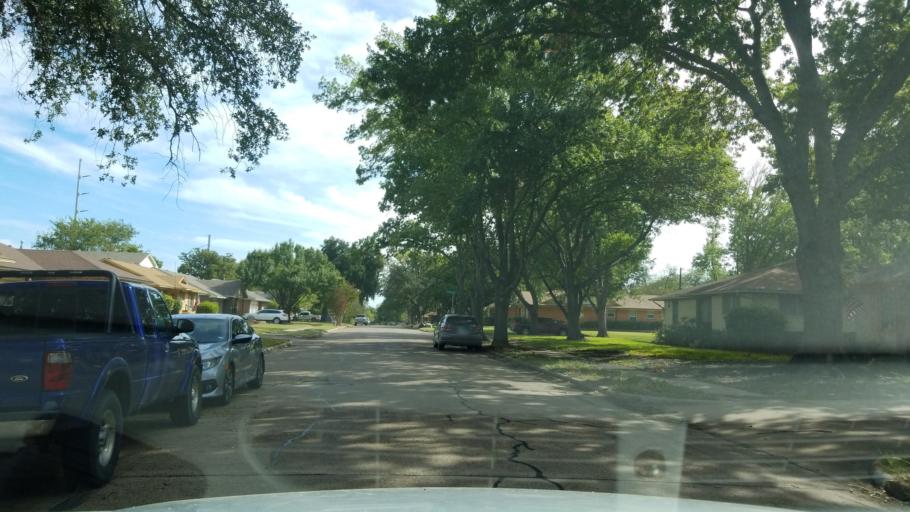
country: US
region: Texas
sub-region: Dallas County
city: Garland
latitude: 32.9038
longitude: -96.6637
